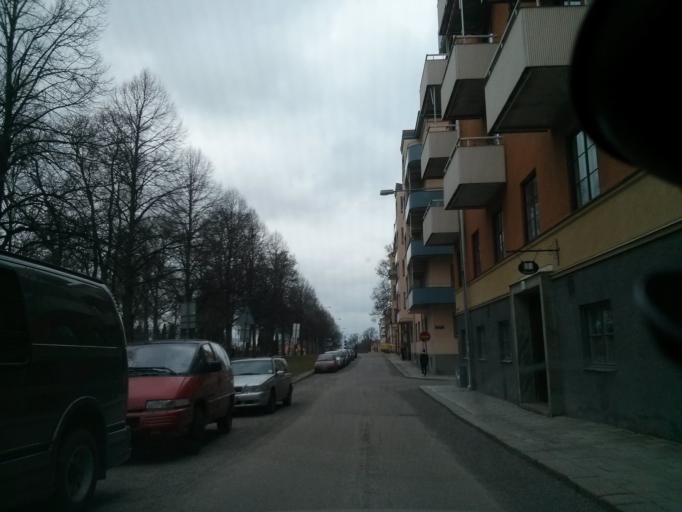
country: SE
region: Uppsala
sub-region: Uppsala Kommun
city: Uppsala
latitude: 59.8560
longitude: 17.6286
